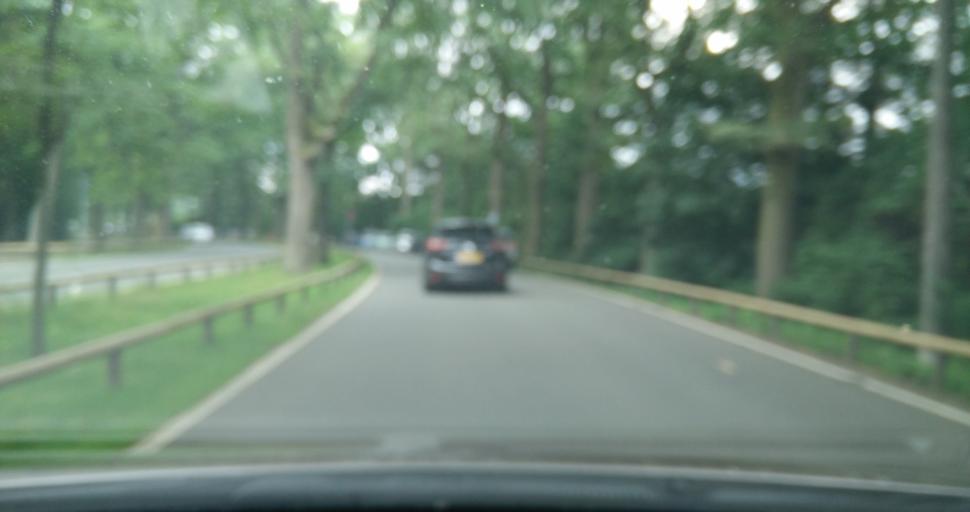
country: DE
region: Bavaria
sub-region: Regierungsbezirk Mittelfranken
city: Nuernberg
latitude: 49.4255
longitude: 11.1273
